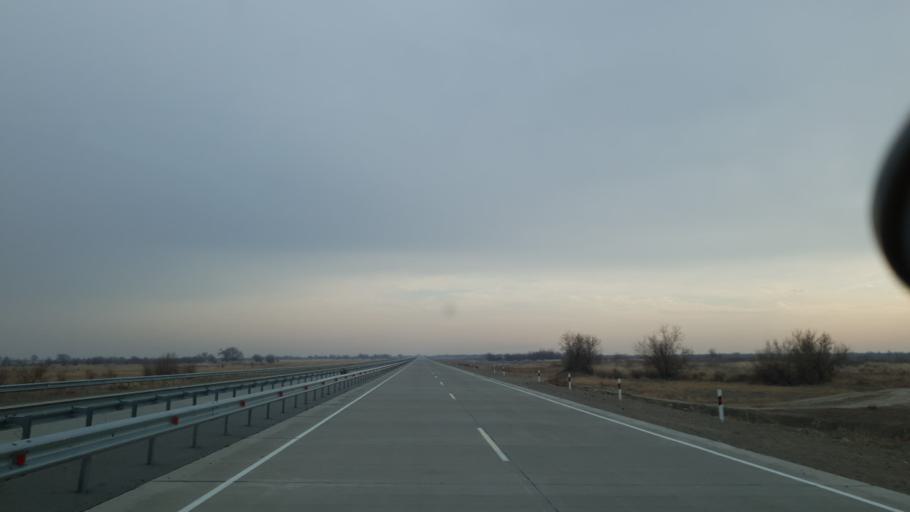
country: KZ
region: Almaty Oblysy
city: Zharkent
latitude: 44.0165
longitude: 79.7743
